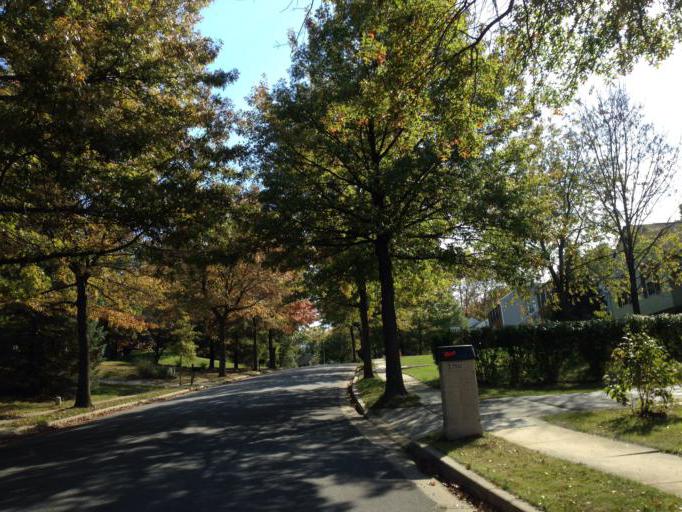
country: US
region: Maryland
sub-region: Howard County
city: Ellicott City
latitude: 39.2565
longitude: -76.8109
